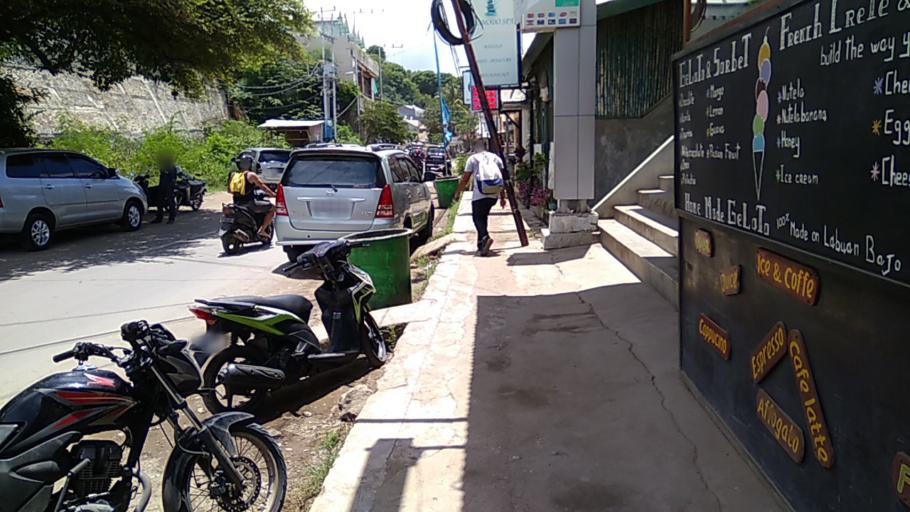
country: ID
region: East Nusa Tenggara
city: Cempa
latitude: -8.4925
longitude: 119.8773
